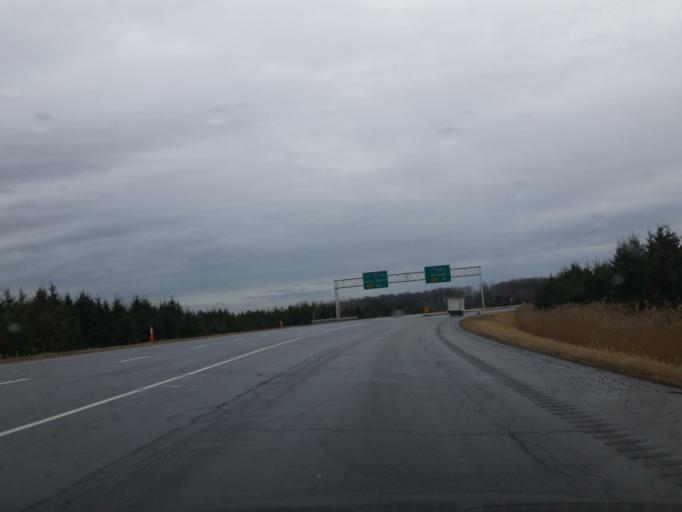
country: CA
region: Quebec
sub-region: Laurentides
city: Saint-Jerome
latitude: 45.7174
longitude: -73.9811
